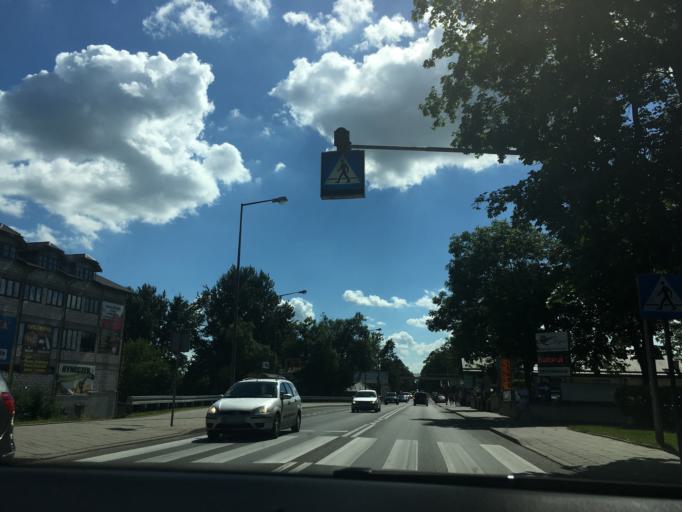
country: PL
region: Podlasie
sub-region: Powiat augustowski
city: Augustow
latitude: 53.8452
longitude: 22.9971
